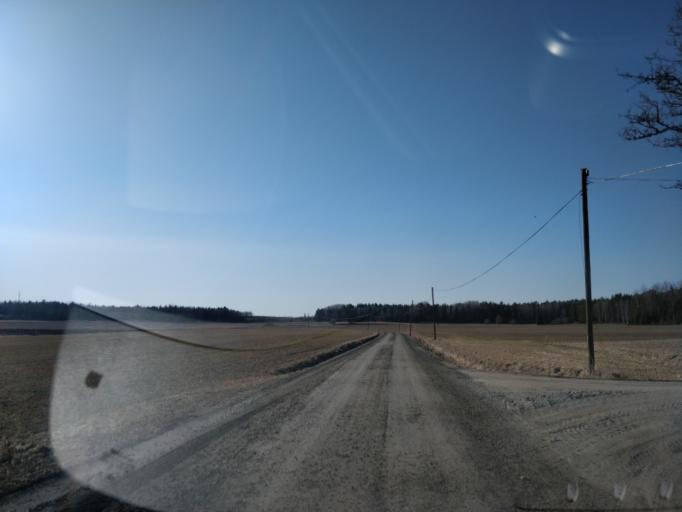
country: SE
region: Uppsala
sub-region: Enkopings Kommun
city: Orsundsbro
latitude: 59.8250
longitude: 17.1343
